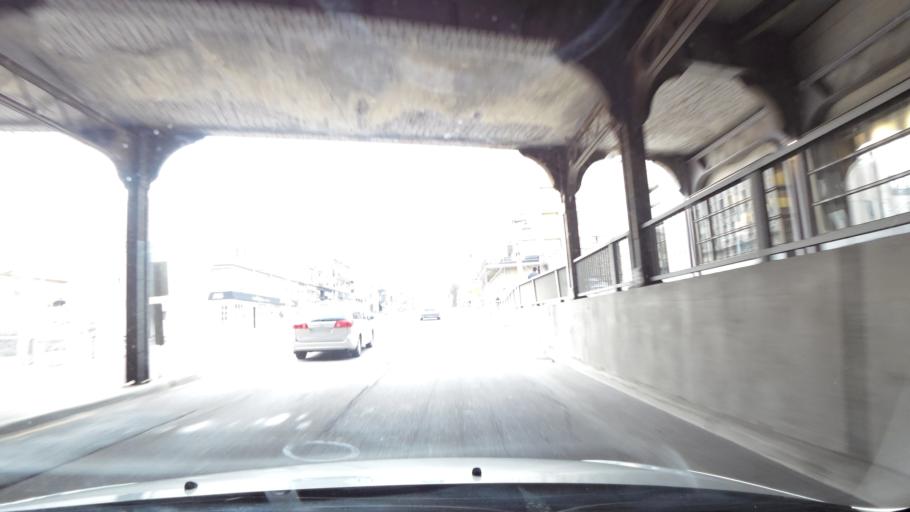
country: CA
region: Ontario
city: Toronto
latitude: 43.6812
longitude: -79.3911
